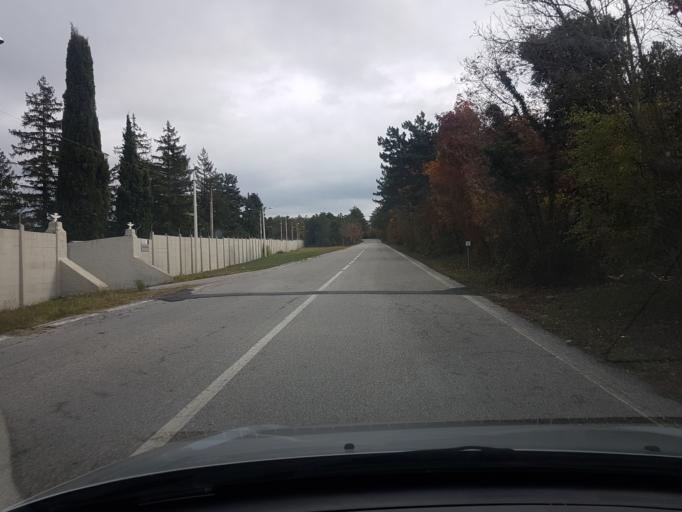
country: IT
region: Friuli Venezia Giulia
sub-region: Provincia di Trieste
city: Prosecco-Contovello
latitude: 45.7032
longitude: 13.7565
